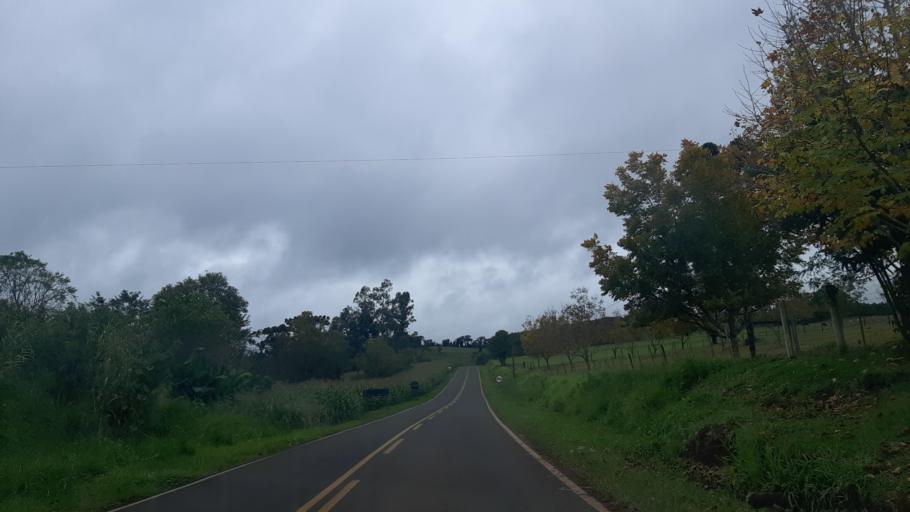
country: BR
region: Parana
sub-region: Ampere
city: Ampere
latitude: -25.9783
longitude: -53.4436
